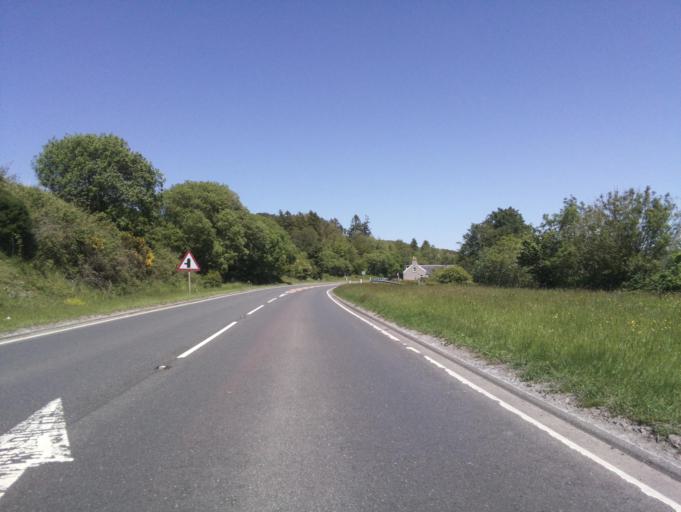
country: GB
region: Scotland
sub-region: The Scottish Borders
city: Hawick
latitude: 55.3824
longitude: -2.8698
